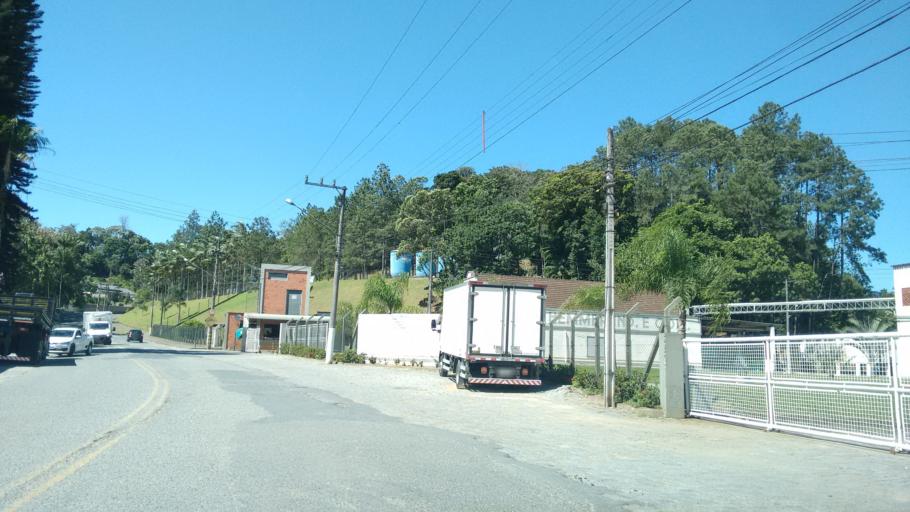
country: BR
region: Santa Catarina
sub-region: Blumenau
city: Blumenau
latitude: -26.8857
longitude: -49.1393
